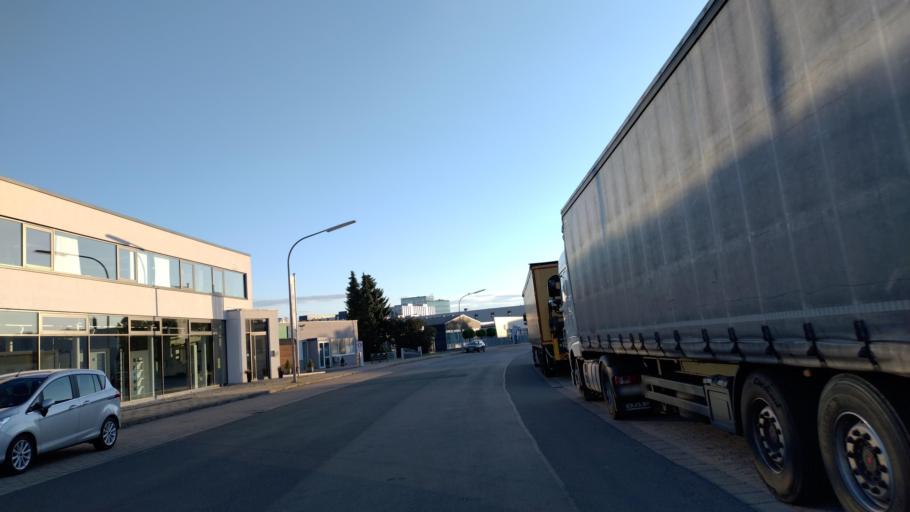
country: DE
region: Bavaria
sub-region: Upper Franconia
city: Bindlach
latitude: 49.9618
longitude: 11.6182
